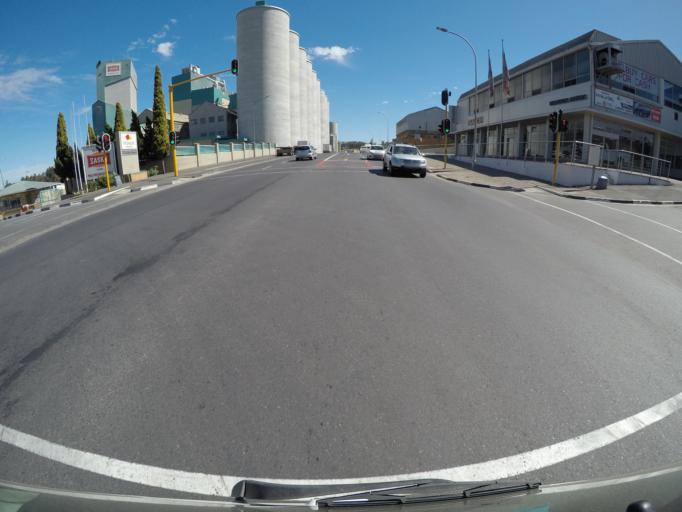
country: ZA
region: Western Cape
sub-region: West Coast District Municipality
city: Malmesbury
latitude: -33.4671
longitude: 18.7242
